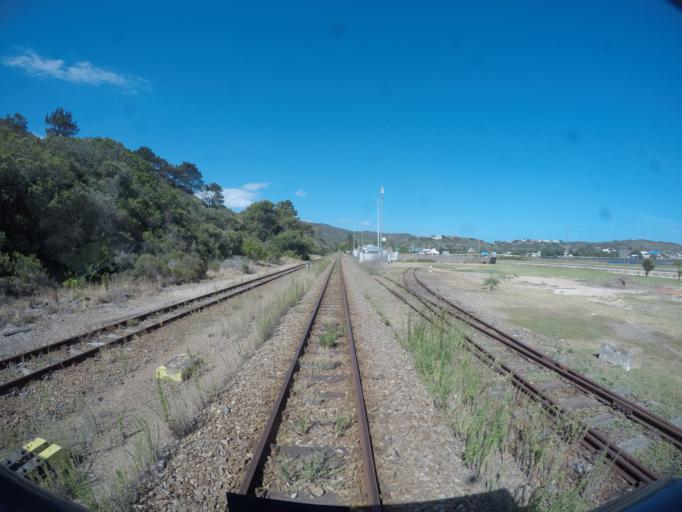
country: ZA
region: Western Cape
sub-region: Eden District Municipality
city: Mossel Bay
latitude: -34.0712
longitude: 22.2862
